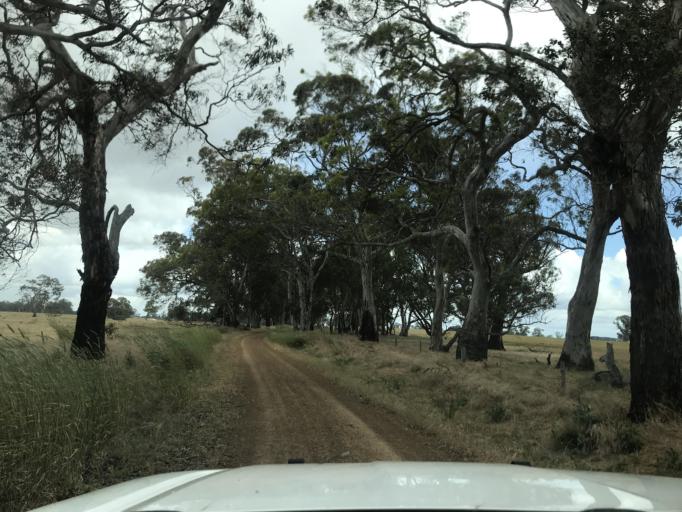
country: AU
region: South Australia
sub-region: Wattle Range
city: Penola
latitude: -37.0877
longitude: 141.3216
